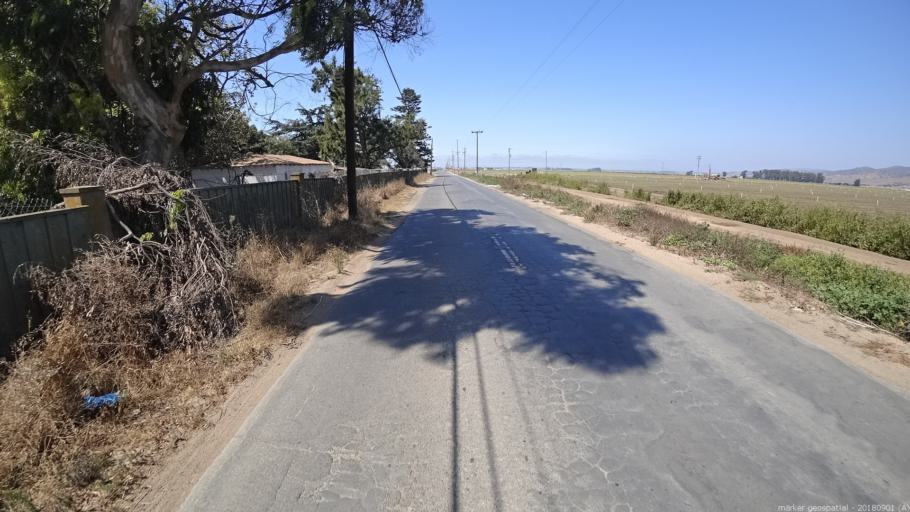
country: US
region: California
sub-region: Monterey County
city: Chualar
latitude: 36.6261
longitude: -121.5288
